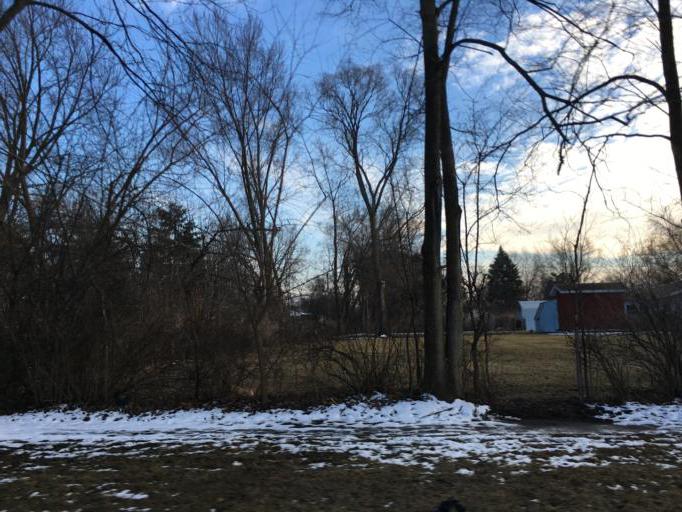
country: US
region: Illinois
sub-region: Cook County
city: Schaumburg
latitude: 42.0406
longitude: -88.0923
